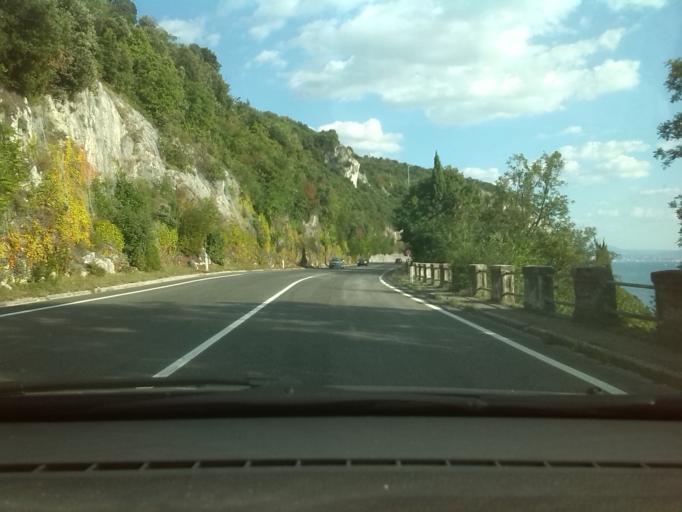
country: IT
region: Friuli Venezia Giulia
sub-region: Provincia di Trieste
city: Aurisina Cave
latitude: 45.7517
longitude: 13.6553
